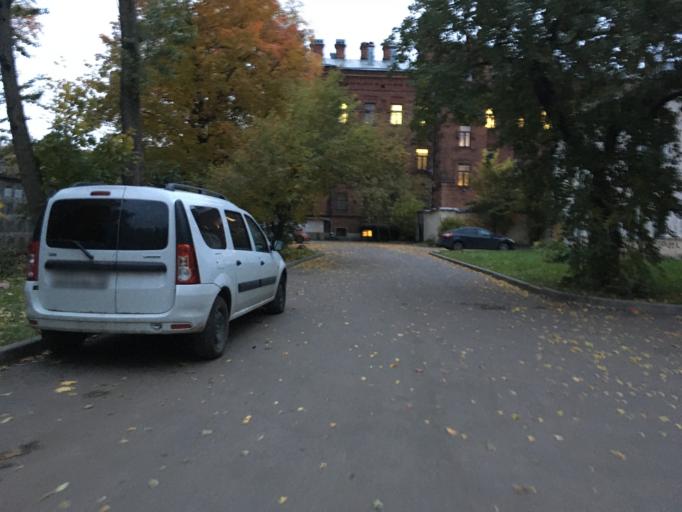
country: RU
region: St.-Petersburg
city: Centralniy
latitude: 59.9042
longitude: 30.3662
